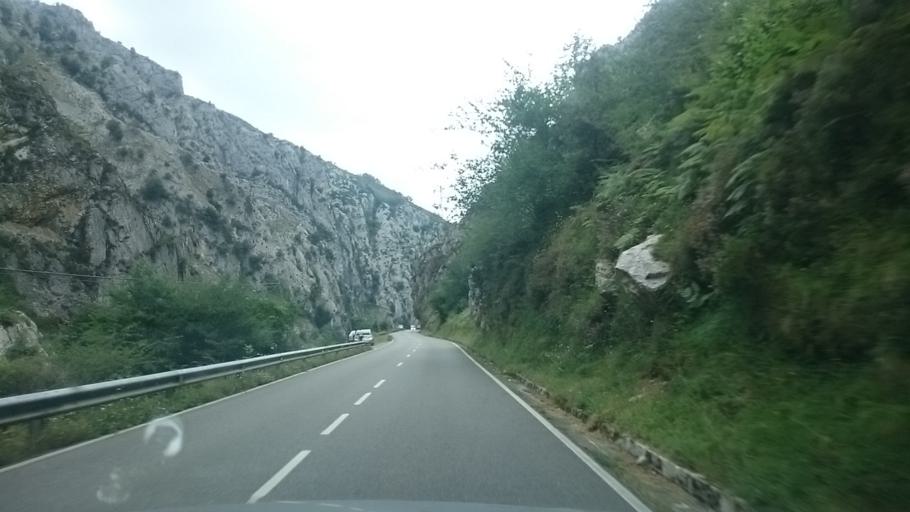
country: ES
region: Asturias
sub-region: Province of Asturias
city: Carrena
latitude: 43.2791
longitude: -4.8344
